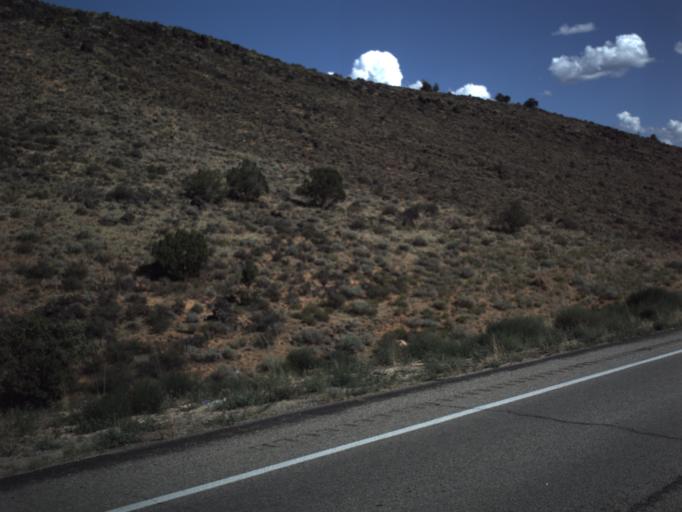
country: US
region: Utah
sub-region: Washington County
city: Toquerville
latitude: 37.2729
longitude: -113.2969
